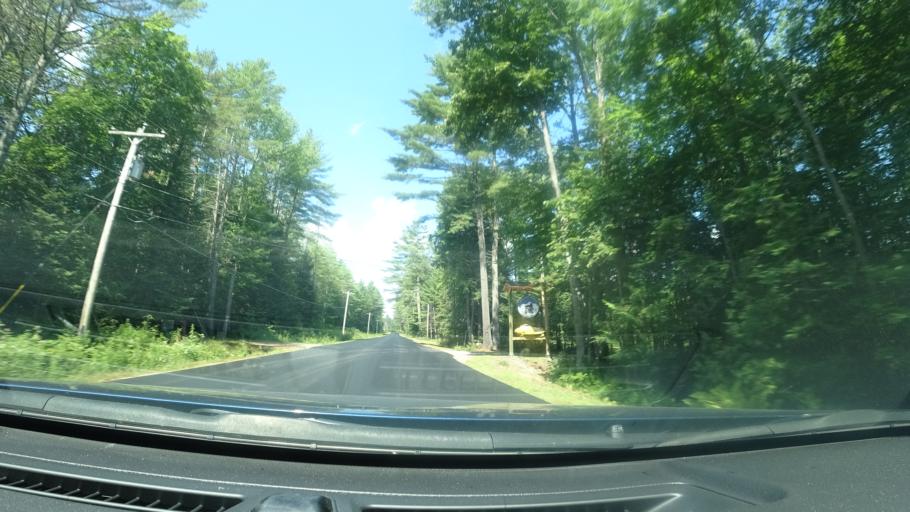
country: US
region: New York
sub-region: Warren County
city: Warrensburg
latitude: 43.6520
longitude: -73.8196
